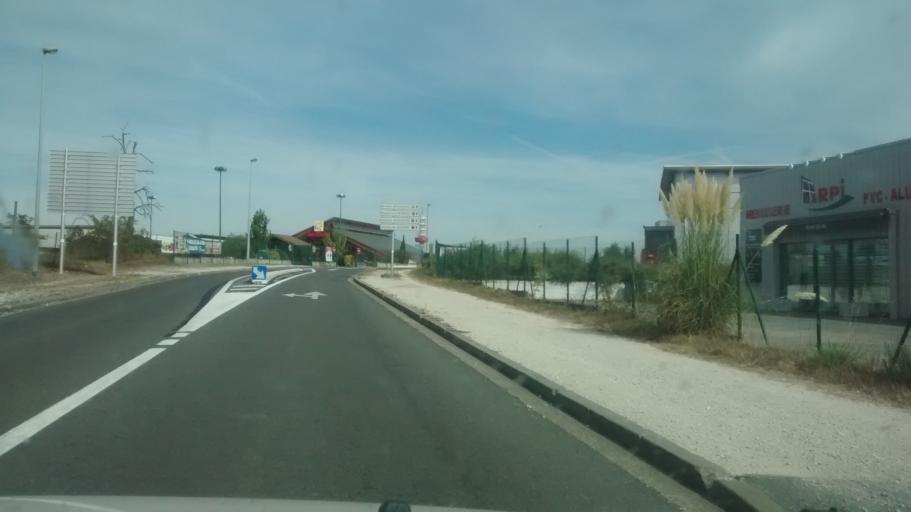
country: FR
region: Aquitaine
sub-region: Departement de la Gironde
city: Floirac
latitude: 44.8425
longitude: -0.4965
